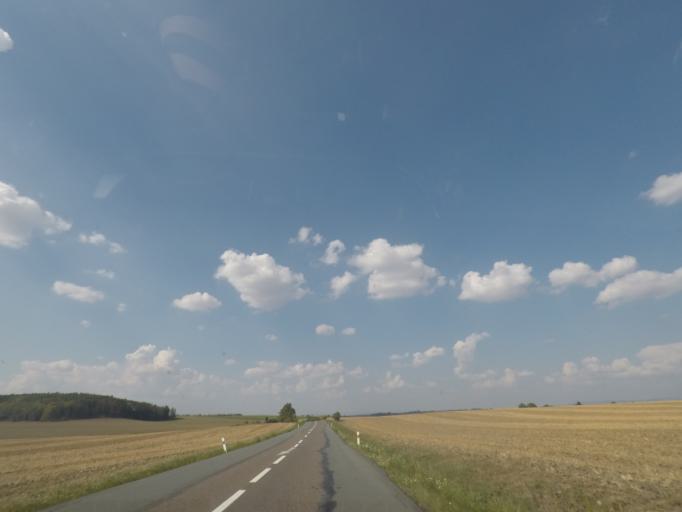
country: CZ
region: Kralovehradecky
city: Dolni Cernilov
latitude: 50.2494
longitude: 15.9651
